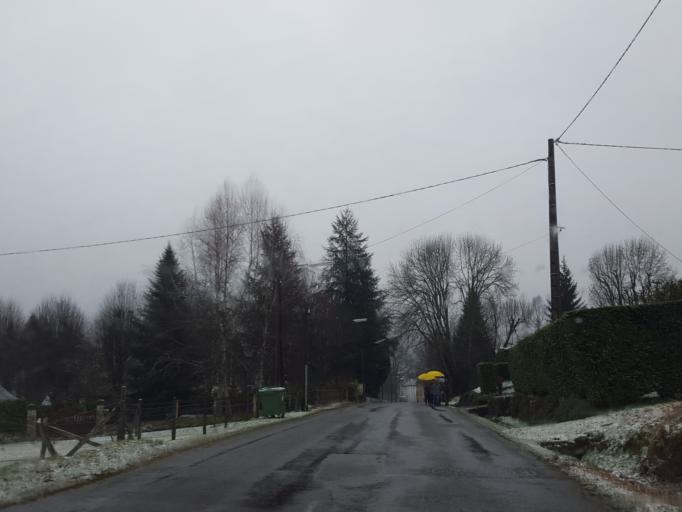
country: FR
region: Midi-Pyrenees
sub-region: Departement de l'Ariege
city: Saint-Girons
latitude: 42.8916
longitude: 1.3416
